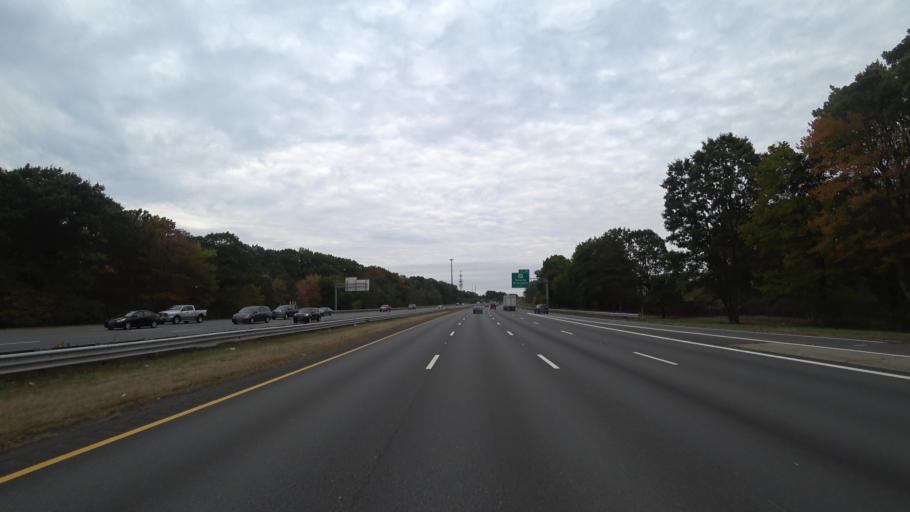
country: US
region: Massachusetts
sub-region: Middlesex County
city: Reading
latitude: 42.5246
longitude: -71.1353
